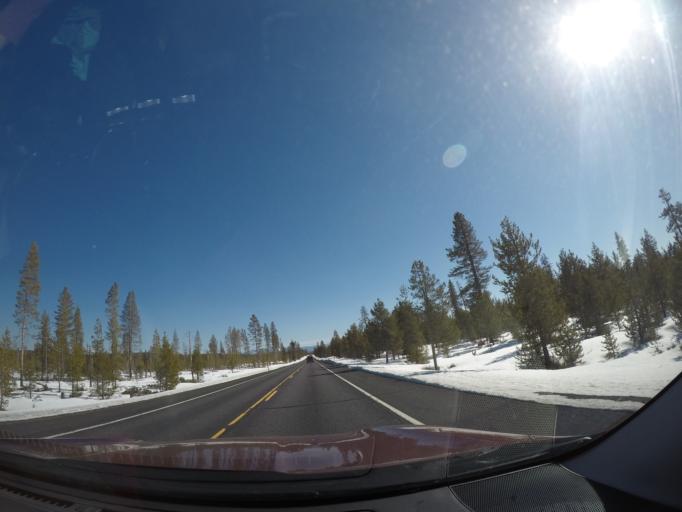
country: US
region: Oregon
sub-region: Deschutes County
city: Three Rivers
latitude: 43.8772
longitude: -121.5608
